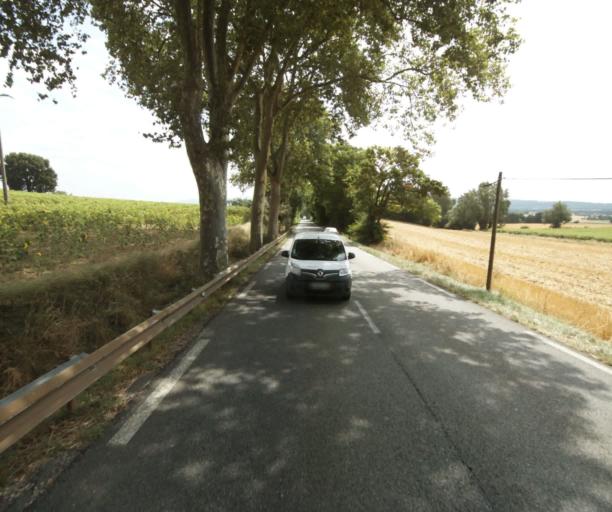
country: FR
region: Midi-Pyrenees
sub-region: Departement de la Haute-Garonne
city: Saint-Felix-Lauragais
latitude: 43.4500
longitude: 1.9049
